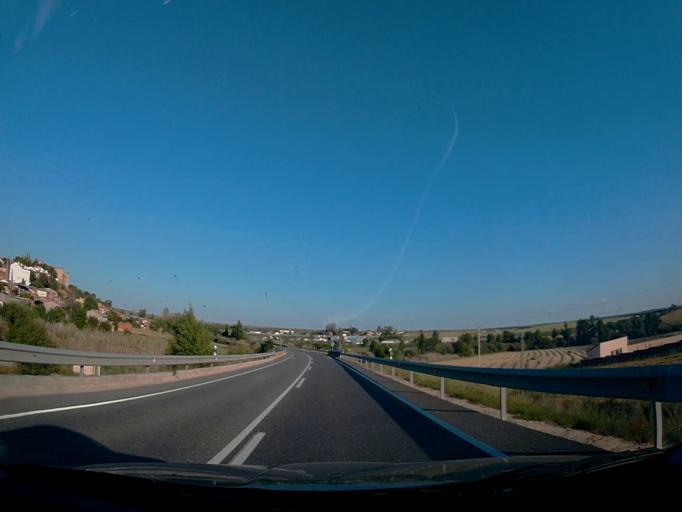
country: ES
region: Castille-La Mancha
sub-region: Province of Toledo
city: Maqueda
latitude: 40.0646
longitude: -4.3762
